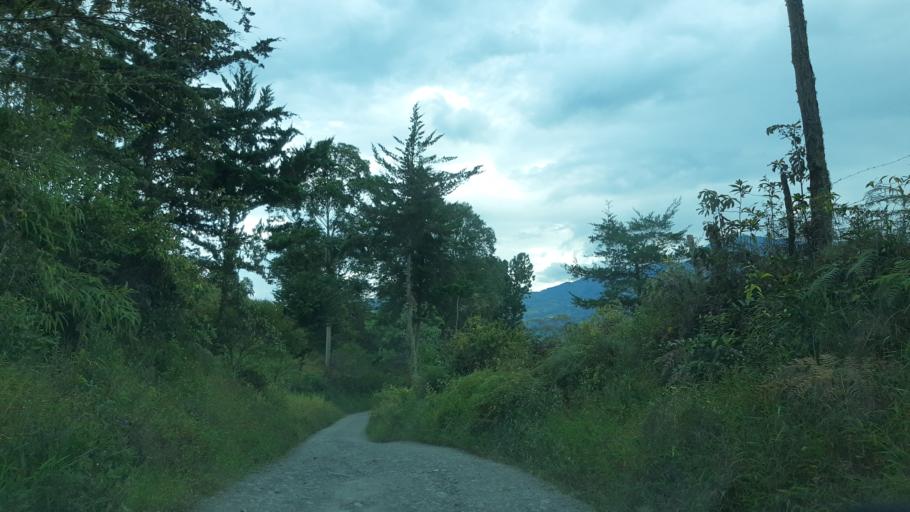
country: CO
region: Boyaca
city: Chivor
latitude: 4.9803
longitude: -73.3229
